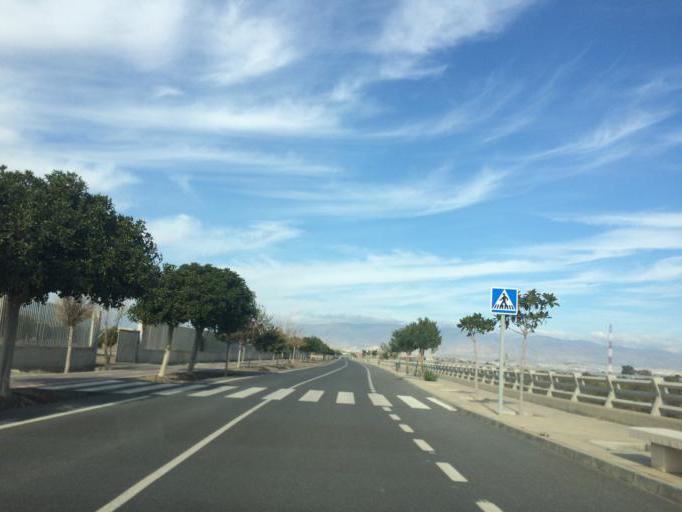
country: ES
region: Andalusia
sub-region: Provincia de Almeria
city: Almeria
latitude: 36.8182
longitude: -2.4296
